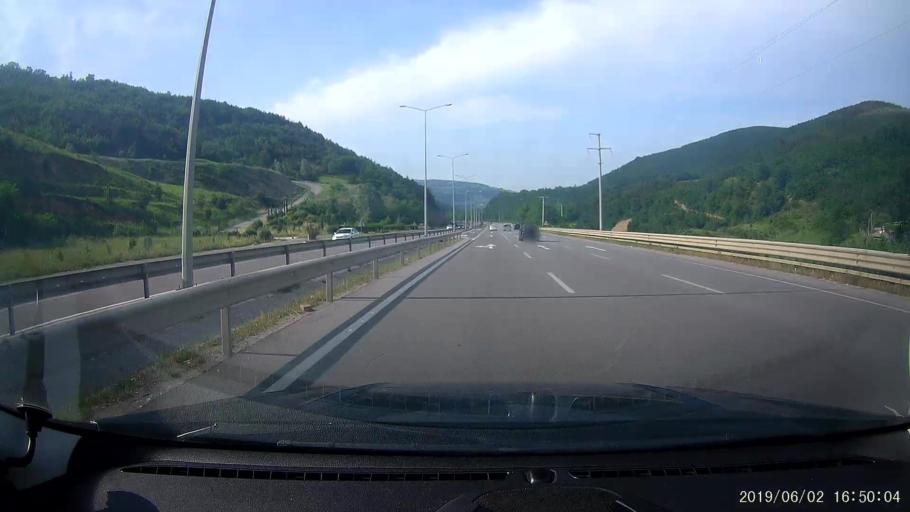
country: TR
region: Samsun
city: Samsun
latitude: 41.2471
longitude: 36.1728
